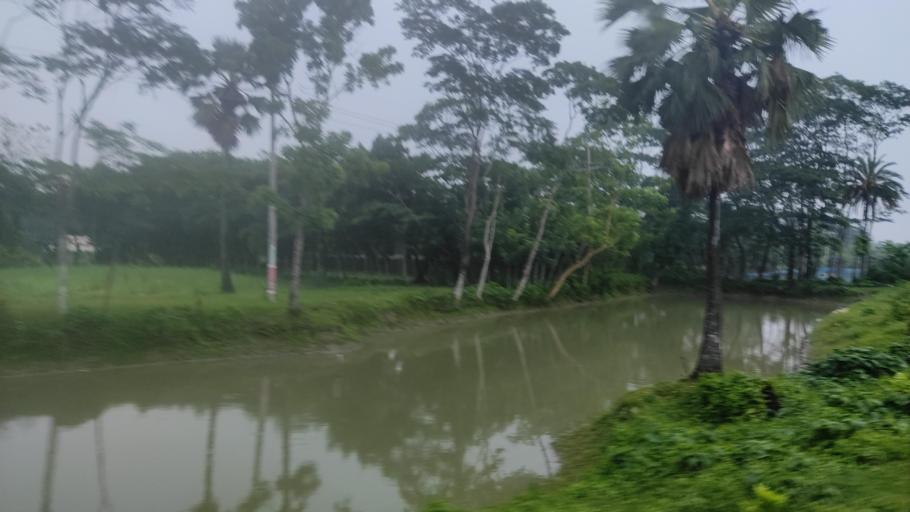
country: BD
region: Barisal
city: Bhandaria
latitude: 22.3004
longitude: 90.3241
